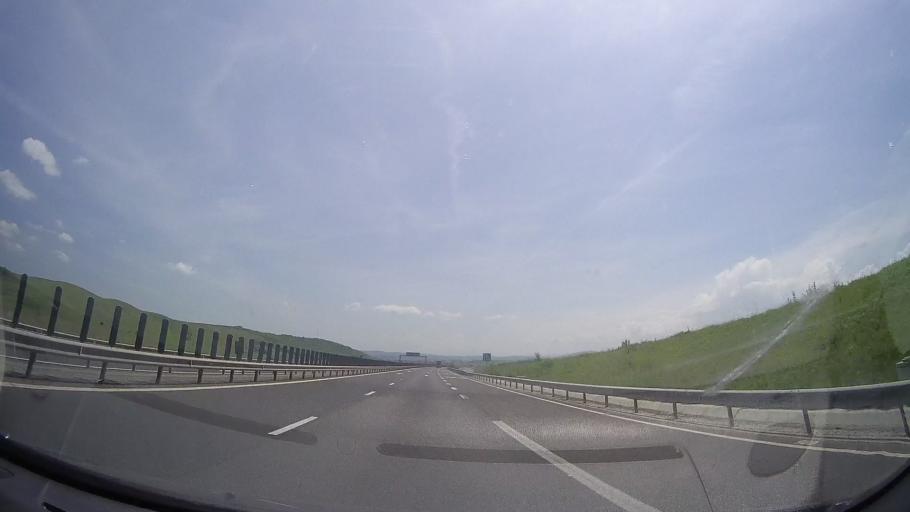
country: RO
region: Alba
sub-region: Comuna Garbova
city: Garbova
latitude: 45.9166
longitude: 23.7274
